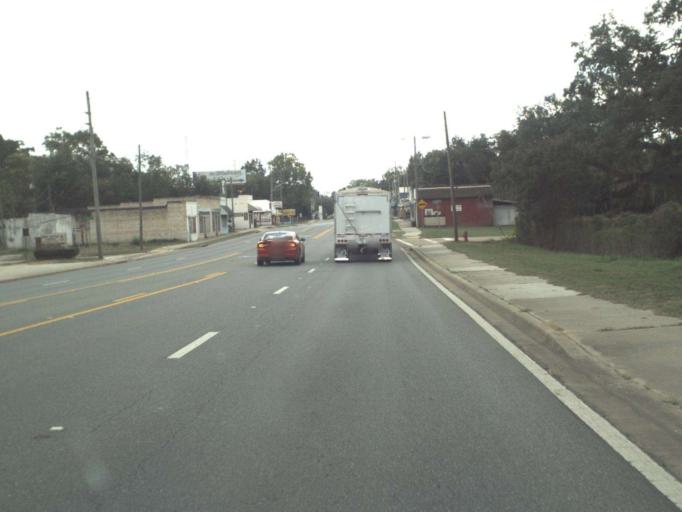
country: US
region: Florida
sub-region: Jackson County
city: Marianna
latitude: 30.7978
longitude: -85.3768
